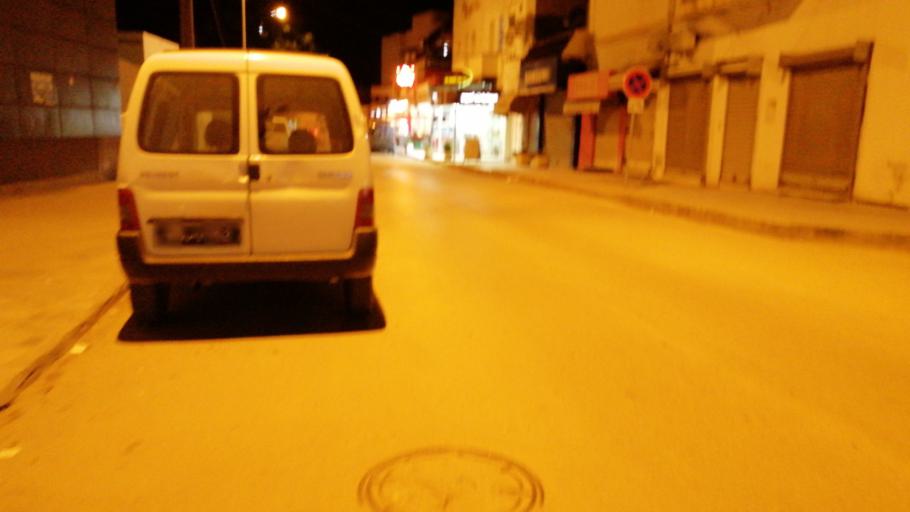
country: TN
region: Al Qayrawan
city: Kairouan
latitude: 35.6719
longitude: 10.1012
